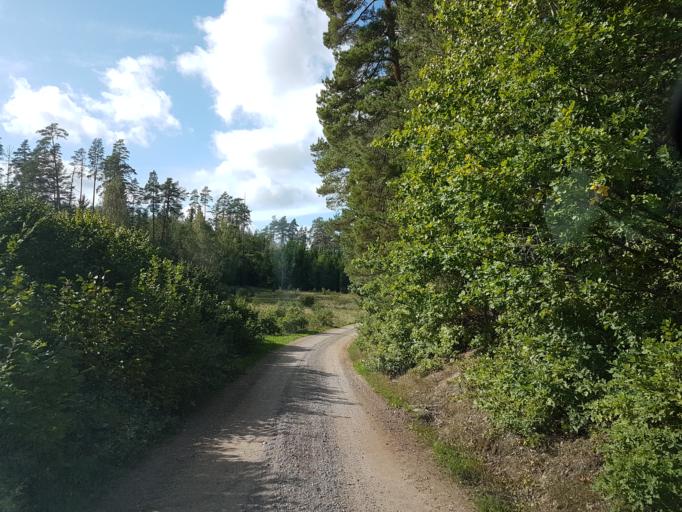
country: SE
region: OEstergoetland
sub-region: Linkopings Kommun
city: Sturefors
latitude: 58.3093
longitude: 15.8489
